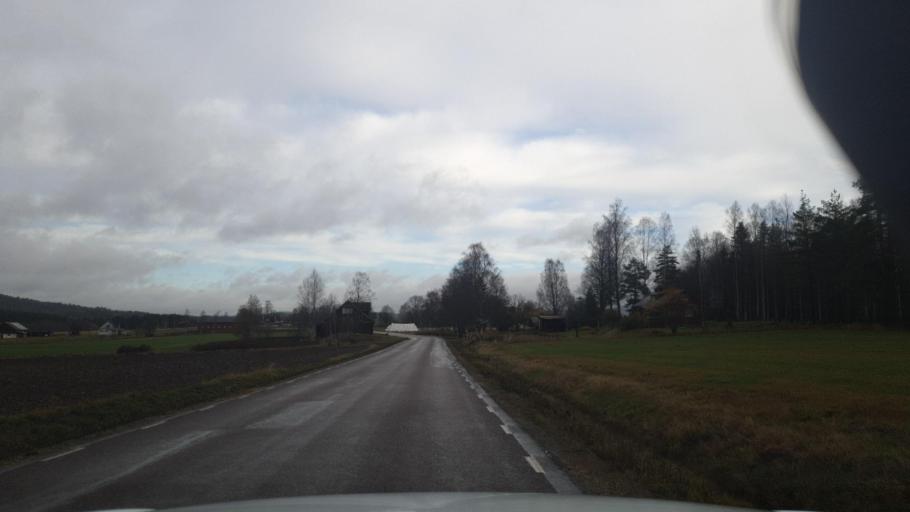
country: SE
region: Vaermland
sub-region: Eda Kommun
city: Charlottenberg
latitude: 59.7634
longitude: 12.1612
